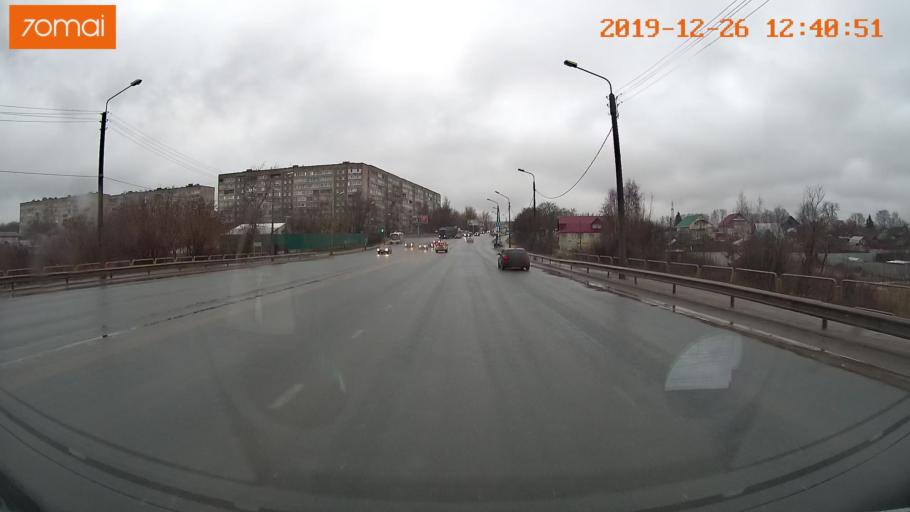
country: RU
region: Vologda
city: Tonshalovo
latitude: 59.1448
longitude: 37.9678
